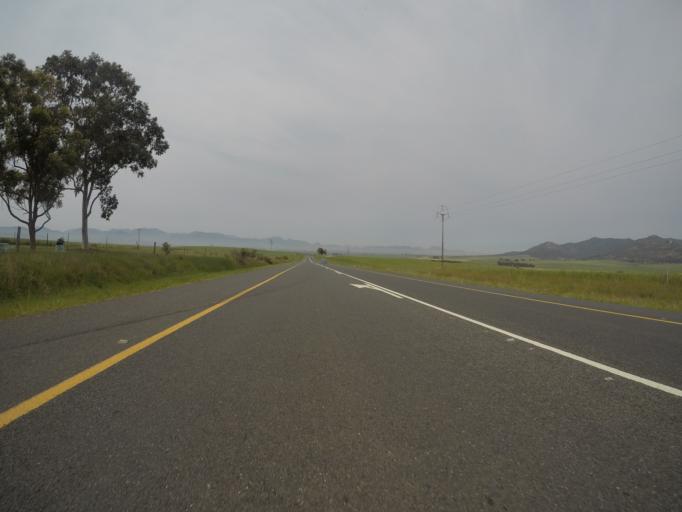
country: ZA
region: Western Cape
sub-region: West Coast District Municipality
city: Malmesbury
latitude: -33.5317
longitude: 18.8515
